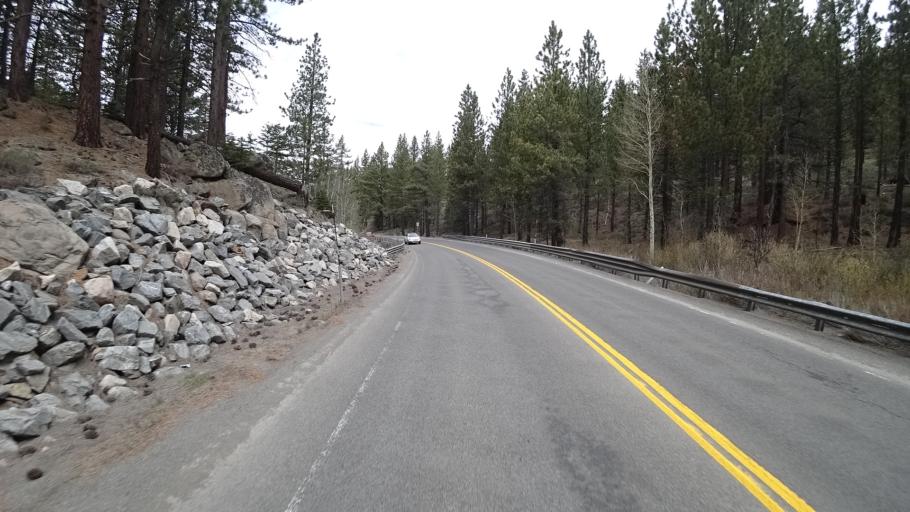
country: US
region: Nevada
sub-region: Douglas County
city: Kingsbury
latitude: 39.1140
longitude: -119.9241
